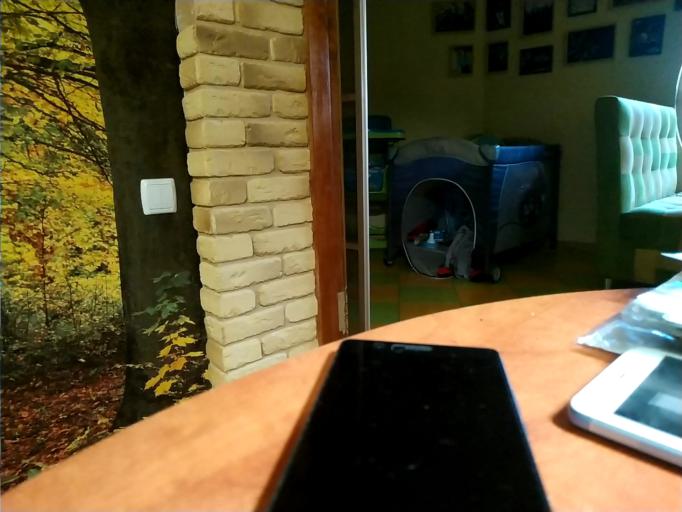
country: RU
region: Orjol
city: Znamenskoye
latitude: 53.5202
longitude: 35.4997
